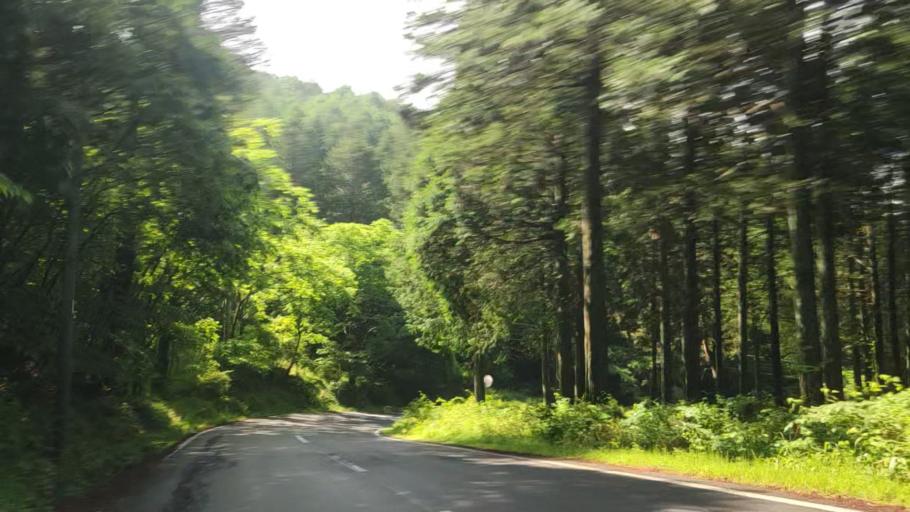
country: JP
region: Nagano
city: Suwa
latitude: 36.0756
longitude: 138.1384
